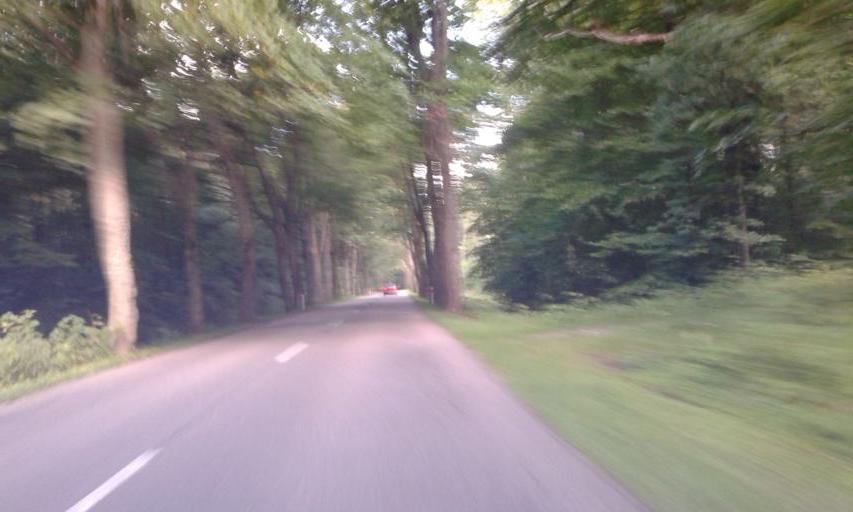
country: PL
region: West Pomeranian Voivodeship
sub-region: Powiat koszalinski
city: Polanow
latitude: 54.2211
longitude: 16.6992
